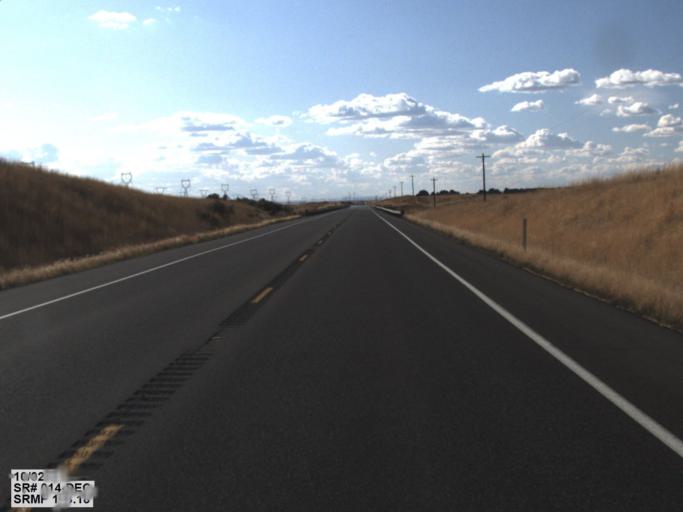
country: US
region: Oregon
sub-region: Morrow County
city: Irrigon
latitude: 45.9459
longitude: -119.4809
